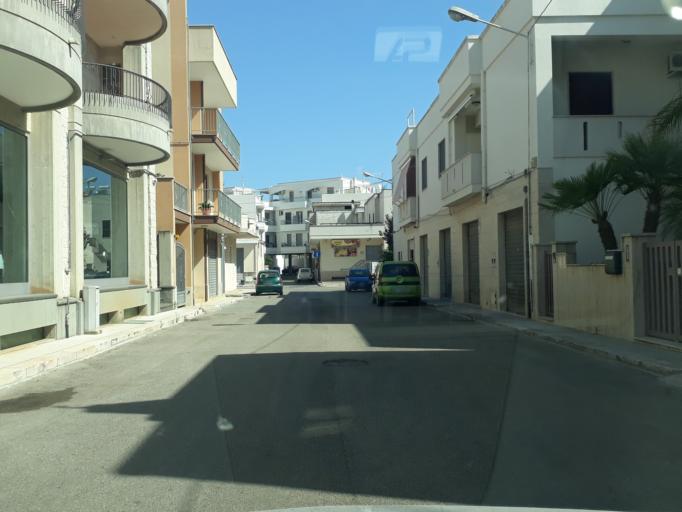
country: IT
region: Apulia
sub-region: Provincia di Brindisi
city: Carovigno
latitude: 40.7128
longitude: 17.6566
